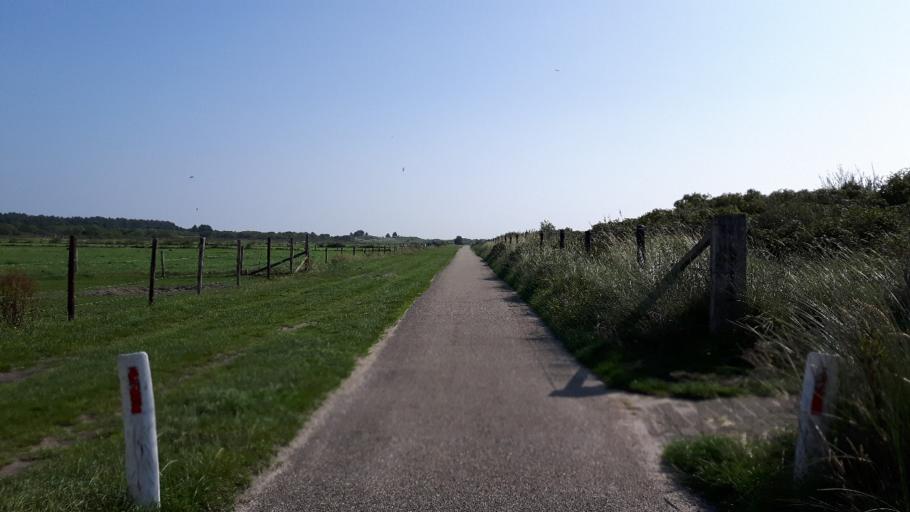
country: NL
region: Friesland
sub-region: Gemeente Ameland
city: Nes
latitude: 53.4555
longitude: 5.8111
